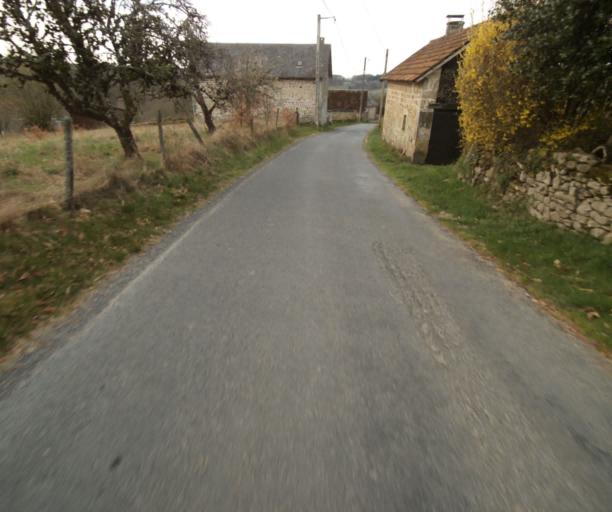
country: FR
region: Limousin
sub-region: Departement de la Correze
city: Correze
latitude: 45.4365
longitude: 1.8255
